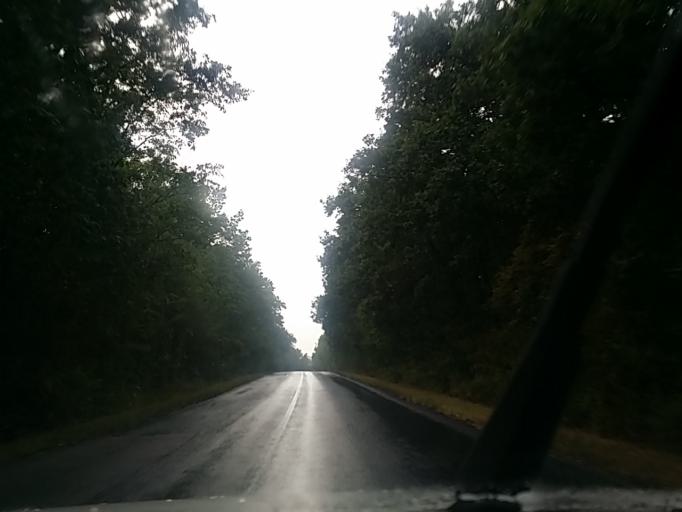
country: HU
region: Pest
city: Paty
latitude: 47.5009
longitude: 18.8750
